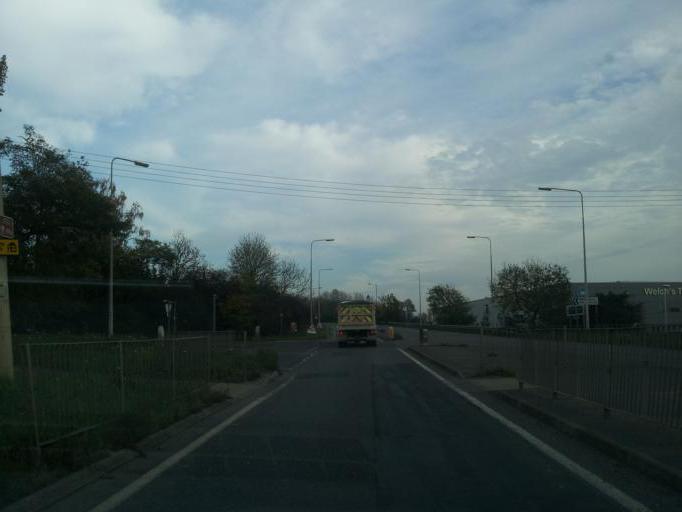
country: GB
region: England
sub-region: Cambridgeshire
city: Duxford
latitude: 52.1022
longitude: 0.1598
